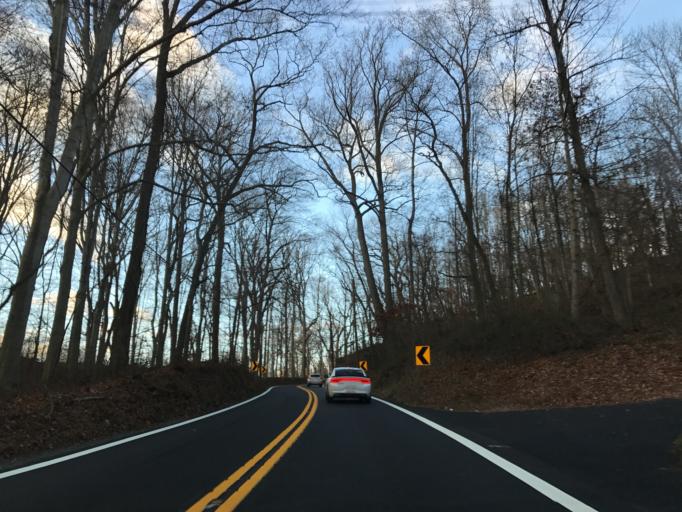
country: US
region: Maryland
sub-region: Harford County
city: Aberdeen
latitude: 39.6264
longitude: -76.2018
